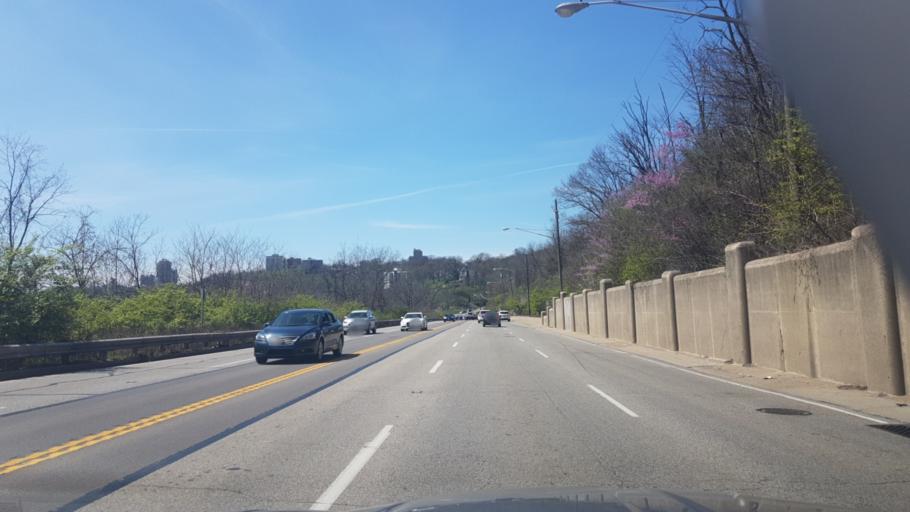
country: US
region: Kentucky
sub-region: Campbell County
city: Dayton
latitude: 39.1247
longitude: -84.4589
